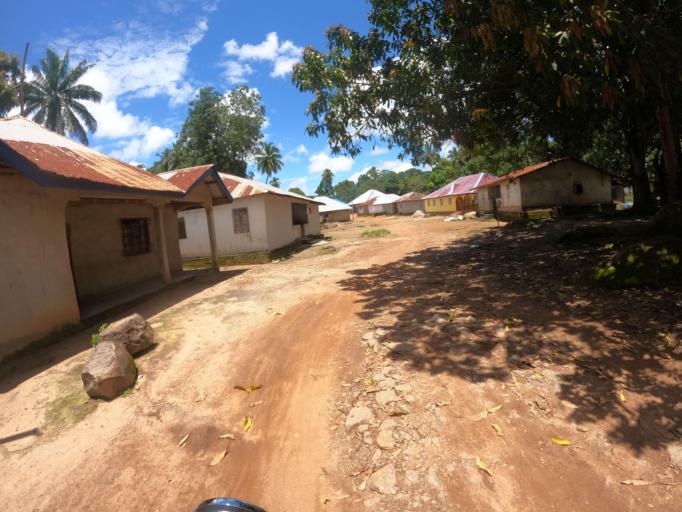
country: SL
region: Northern Province
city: Makeni
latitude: 8.8909
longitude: -12.0705
